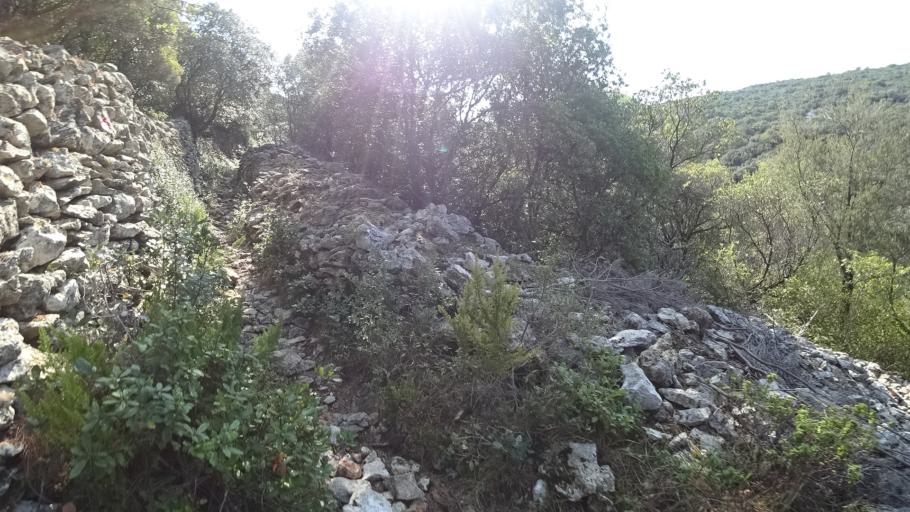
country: HR
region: Primorsko-Goranska
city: Mali Losinj
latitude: 44.5005
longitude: 14.5240
